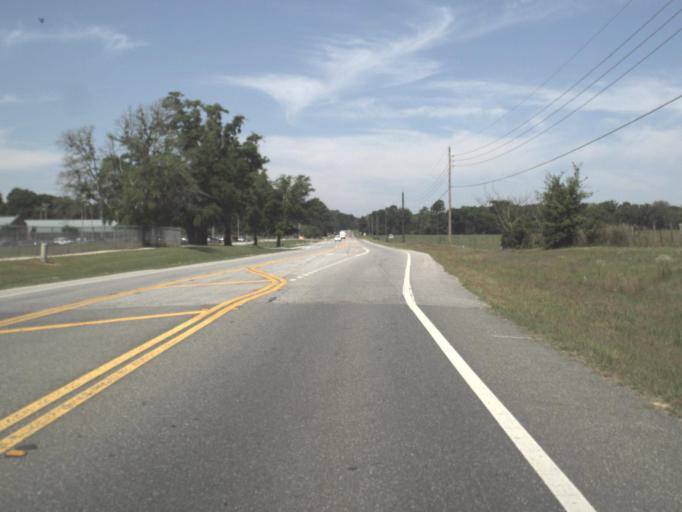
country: US
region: Florida
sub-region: Jackson County
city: Marianna
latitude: 30.8124
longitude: -85.1965
